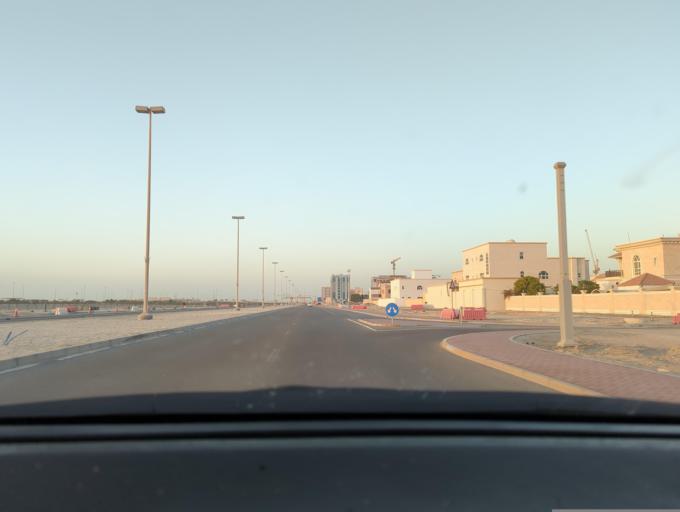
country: AE
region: Abu Dhabi
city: Abu Dhabi
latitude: 24.3108
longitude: 54.5307
